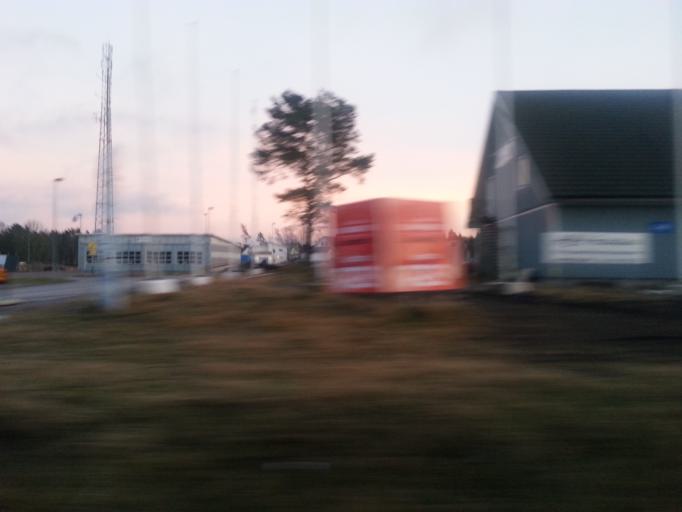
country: SE
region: Vaestra Goetaland
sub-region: Partille Kommun
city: Furulund
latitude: 57.7035
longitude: 12.1487
